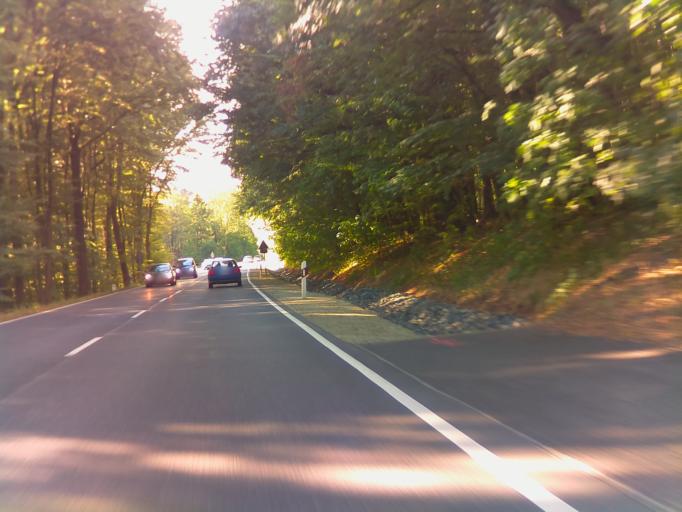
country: DE
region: Hesse
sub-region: Regierungsbezirk Kassel
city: Poppenhausen
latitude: 50.5156
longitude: 9.8535
